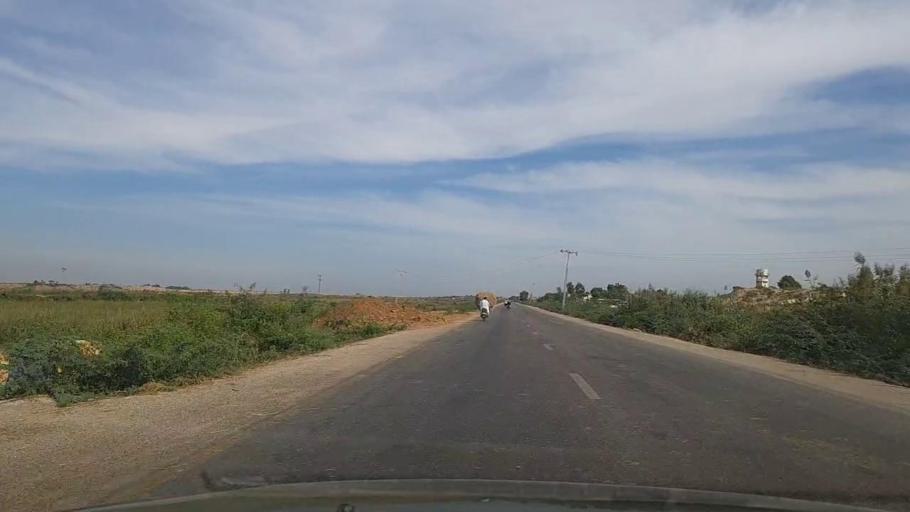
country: PK
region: Sindh
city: Thatta
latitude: 24.8175
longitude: 67.9825
